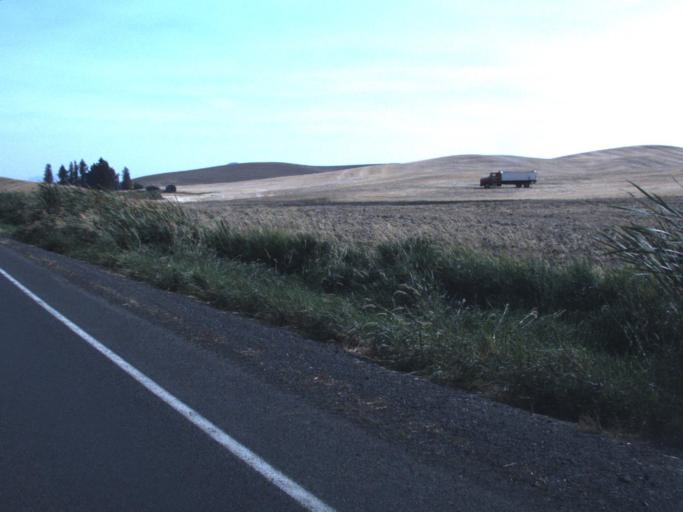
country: US
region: Idaho
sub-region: Benewah County
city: Plummer
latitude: 47.1964
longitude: -117.1388
